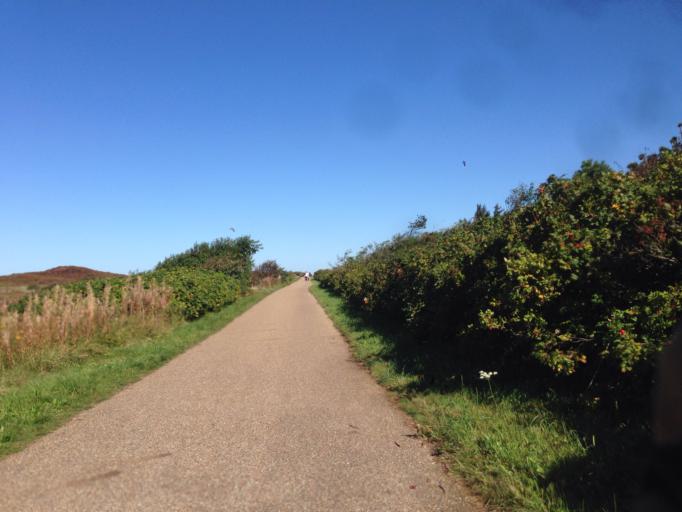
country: DE
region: Schleswig-Holstein
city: Tinnum
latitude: 54.9504
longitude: 8.3367
